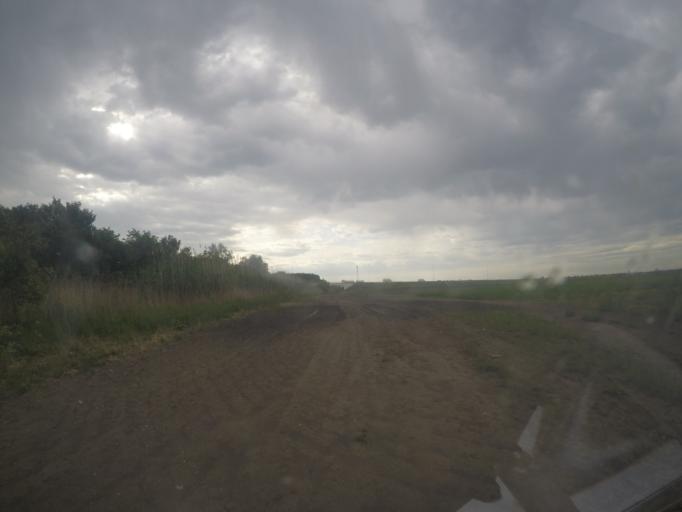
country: RS
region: Central Serbia
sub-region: Belgrade
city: Zemun
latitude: 44.8908
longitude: 20.4036
